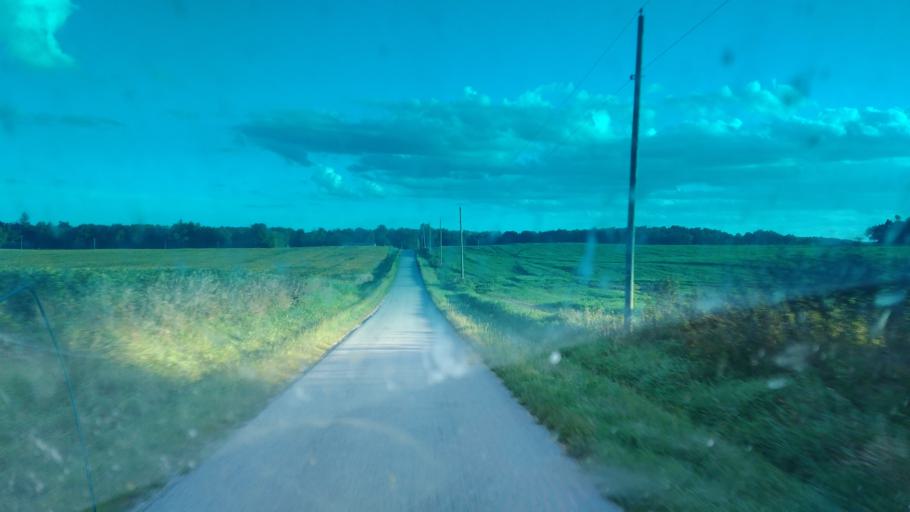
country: US
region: Ohio
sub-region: Wyandot County
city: Upper Sandusky
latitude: 40.8461
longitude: -83.1507
